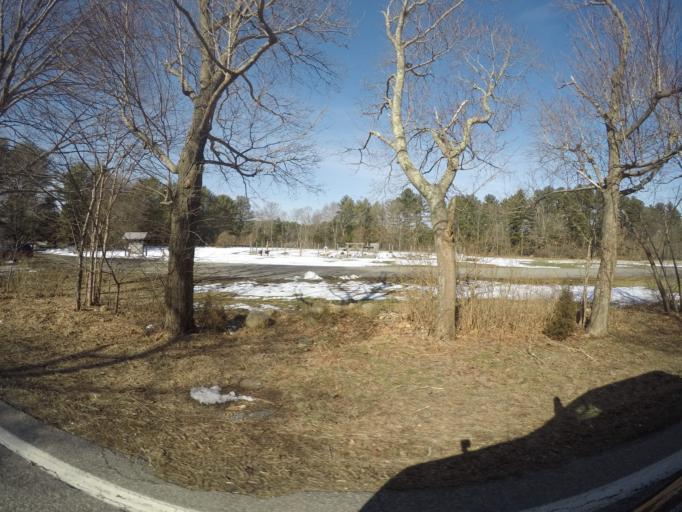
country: US
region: Massachusetts
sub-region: Bristol County
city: Easton
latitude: 42.0060
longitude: -71.1205
